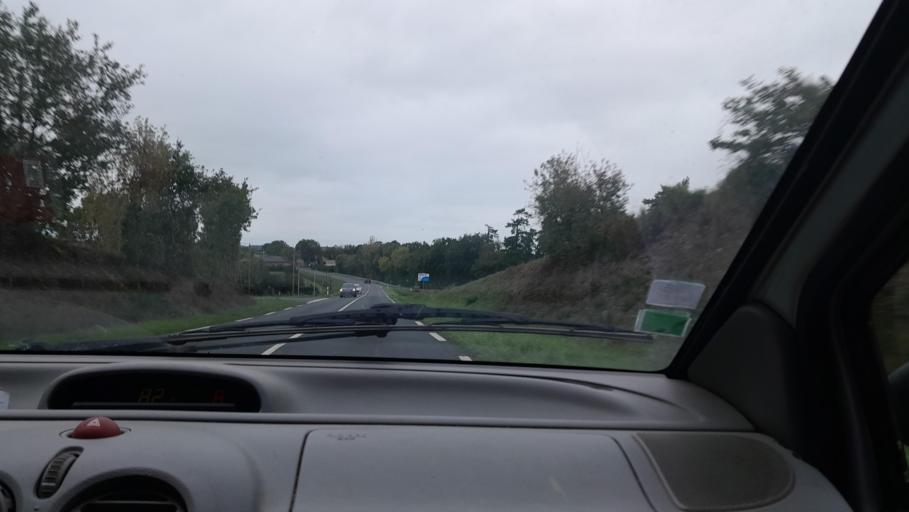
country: FR
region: Pays de la Loire
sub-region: Departement de la Loire-Atlantique
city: Saint-Mars-la-Jaille
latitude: 47.5068
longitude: -1.1828
